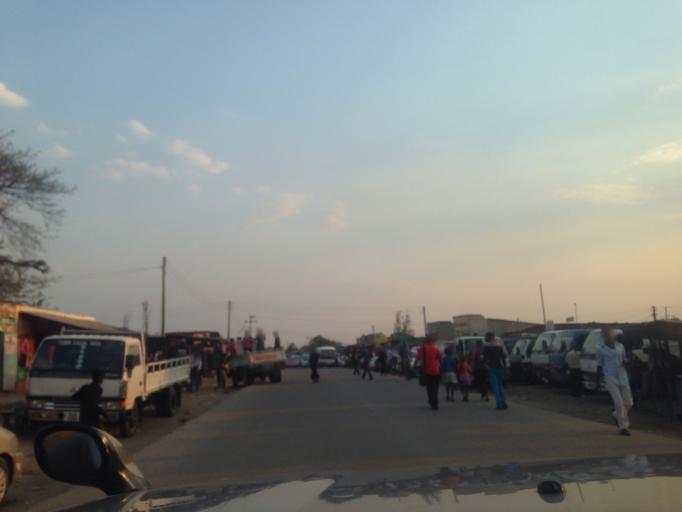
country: ZM
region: Lusaka
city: Lusaka
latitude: -15.4010
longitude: 28.3561
